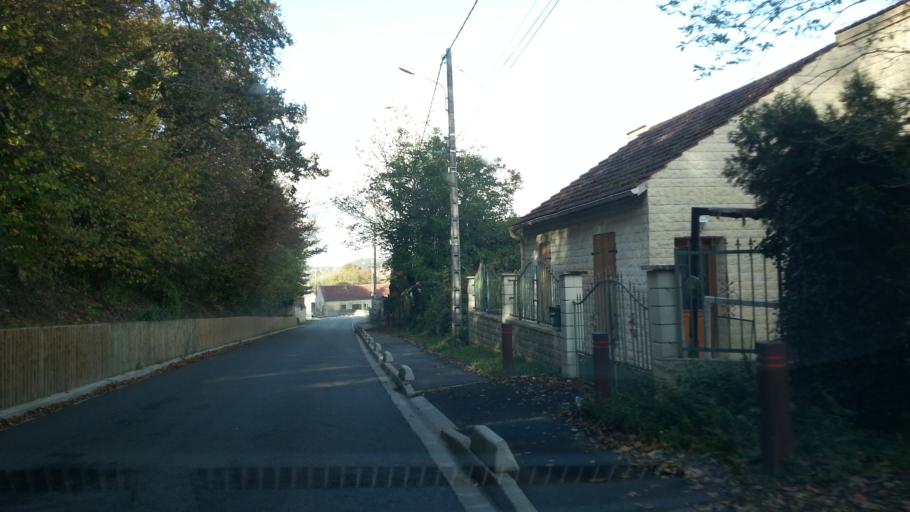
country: FR
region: Picardie
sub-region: Departement de l'Oise
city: Thiverny
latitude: 49.2530
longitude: 2.4035
